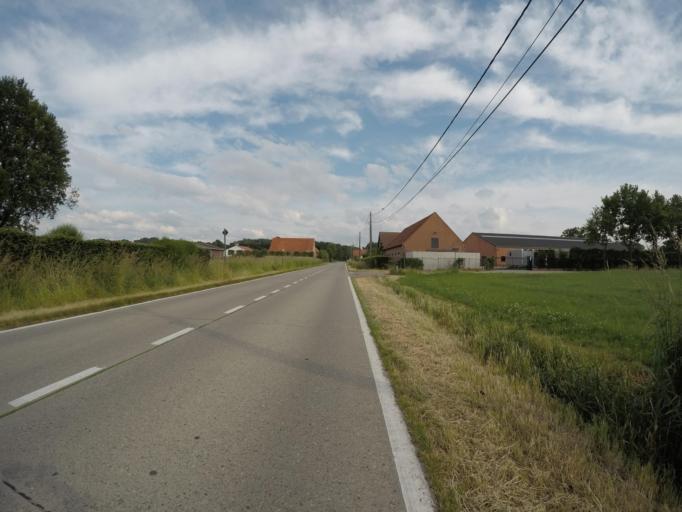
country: BE
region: Flanders
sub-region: Provincie Antwerpen
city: Brecht
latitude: 51.3610
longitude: 4.6883
